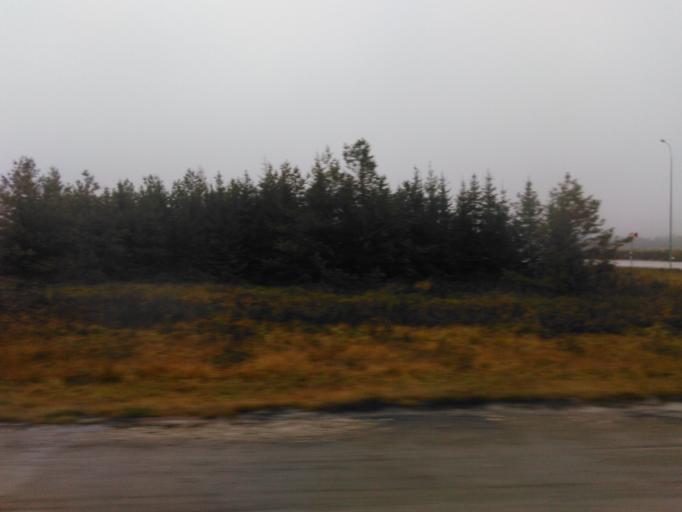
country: RU
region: Tatarstan
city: Sviyazhsk
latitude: 55.7271
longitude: 48.7590
